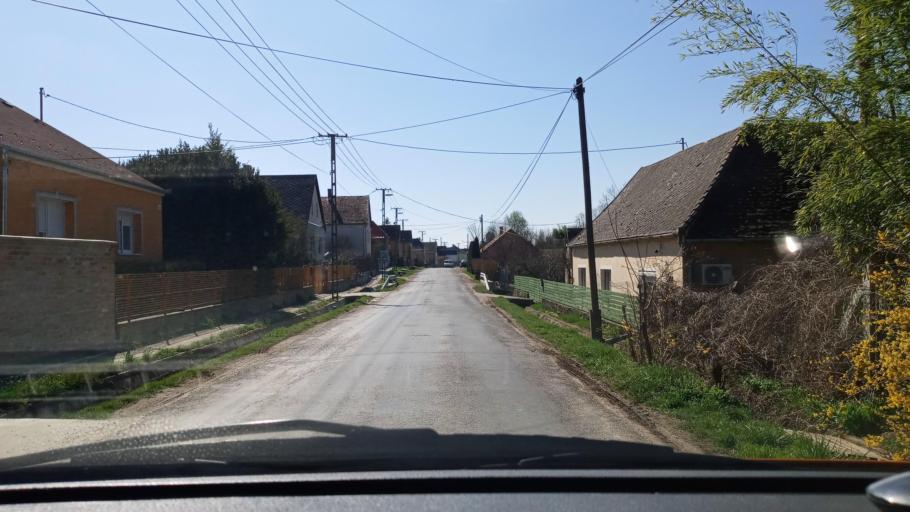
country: HU
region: Baranya
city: Kozarmisleny
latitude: 46.0623
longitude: 18.3738
